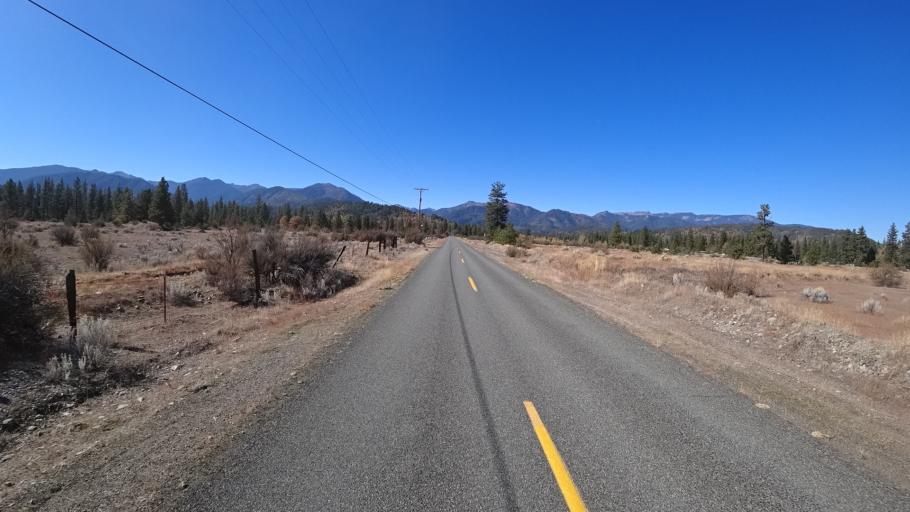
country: US
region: California
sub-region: Siskiyou County
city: Yreka
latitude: 41.5401
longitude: -122.9105
